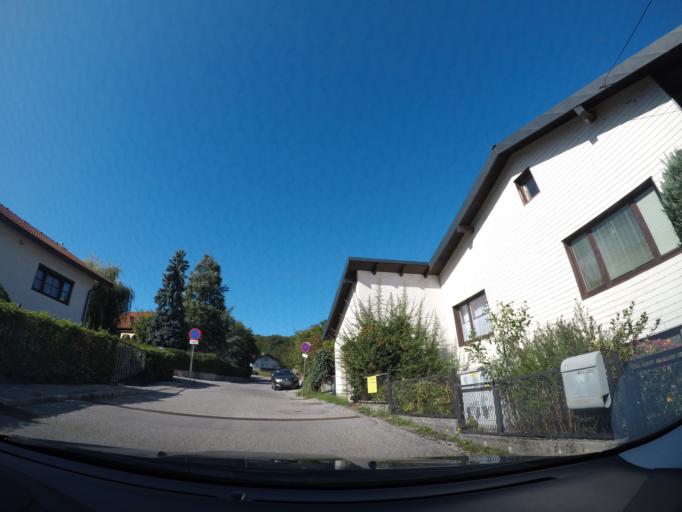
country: AT
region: Lower Austria
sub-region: Politischer Bezirk Wien-Umgebung
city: Pressbaum
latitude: 48.1883
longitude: 16.1040
